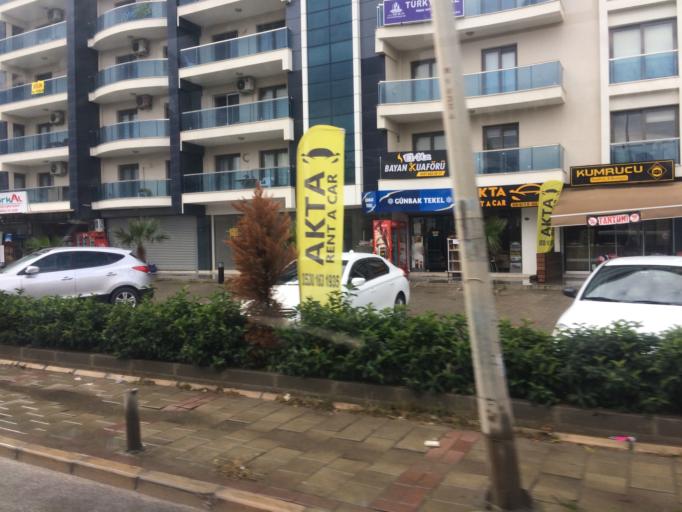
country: TR
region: Izmir
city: Karsiyaka
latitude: 38.5166
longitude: 27.0418
